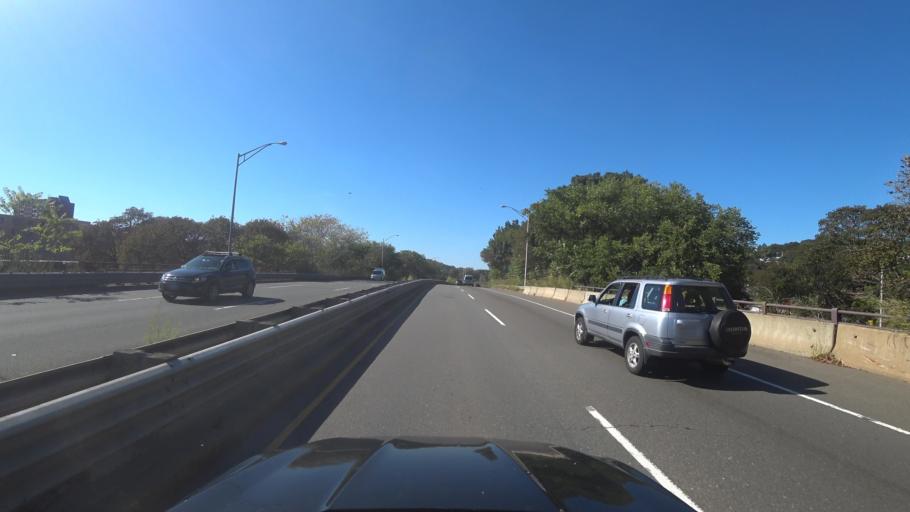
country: US
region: Massachusetts
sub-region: Suffolk County
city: Revere
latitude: 42.4038
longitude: -71.0165
